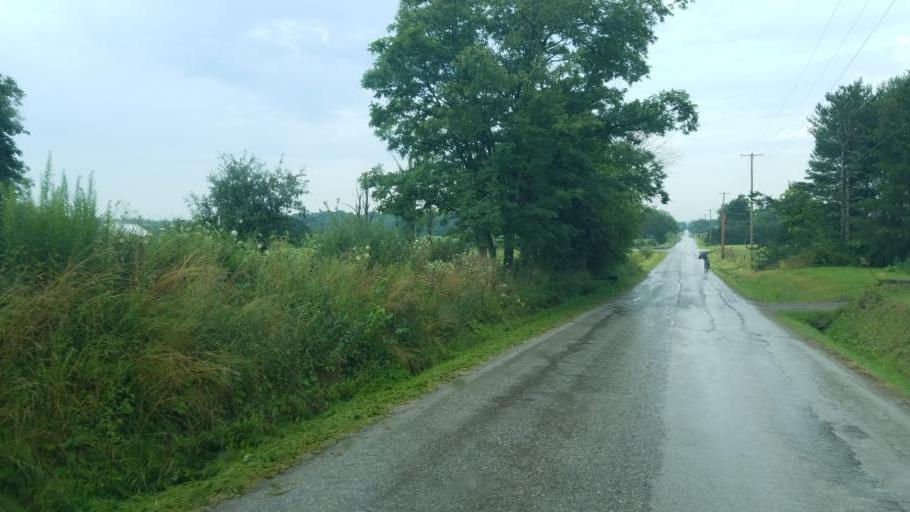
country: US
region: Ohio
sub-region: Geauga County
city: Middlefield
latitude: 41.4792
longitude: -81.0199
